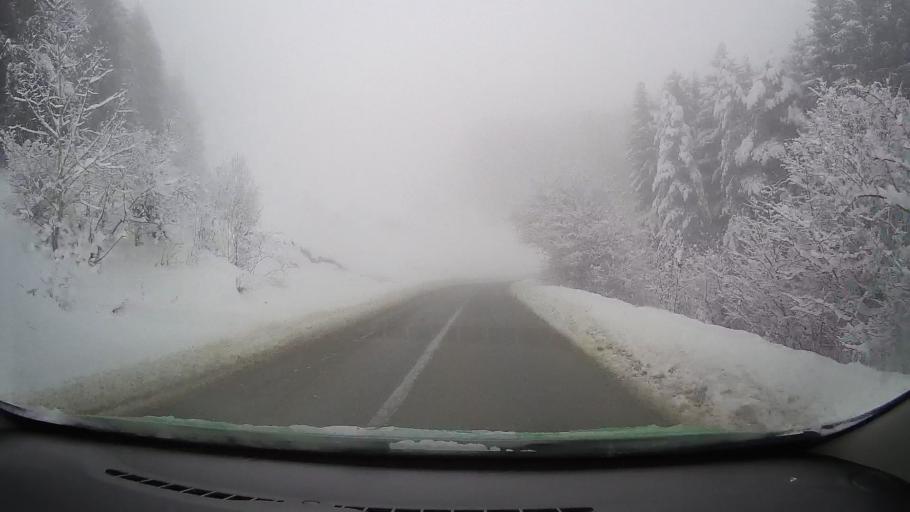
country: RO
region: Sibiu
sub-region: Comuna Jina
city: Jina
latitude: 45.7919
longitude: 23.6997
